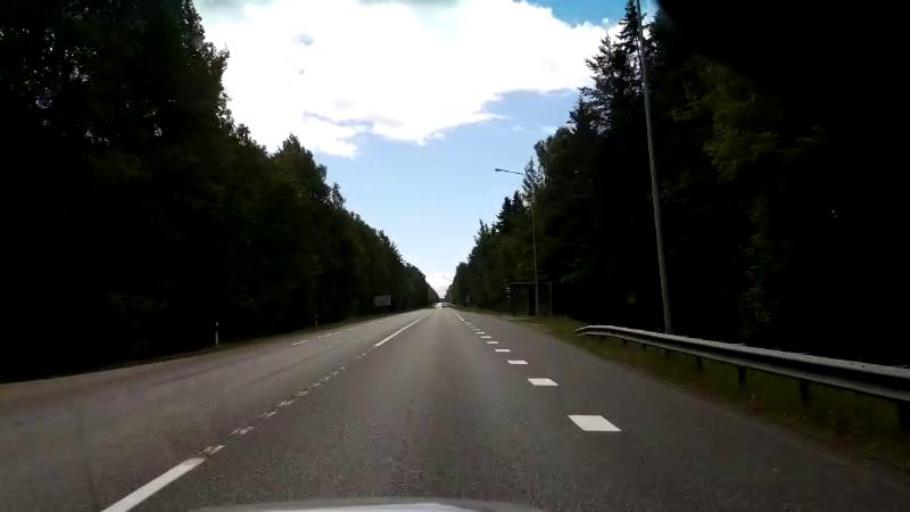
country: LV
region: Saulkrastu
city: Saulkrasti
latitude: 57.4892
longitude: 24.4321
